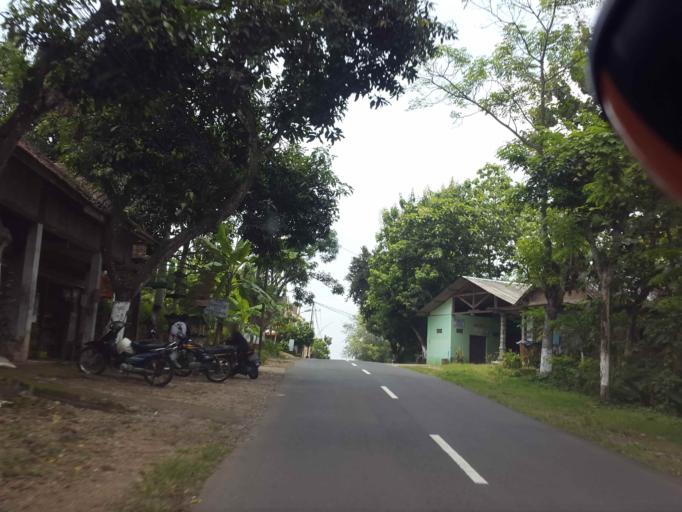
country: ID
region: East Java
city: Ponorogo
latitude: -7.7417
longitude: 111.3405
